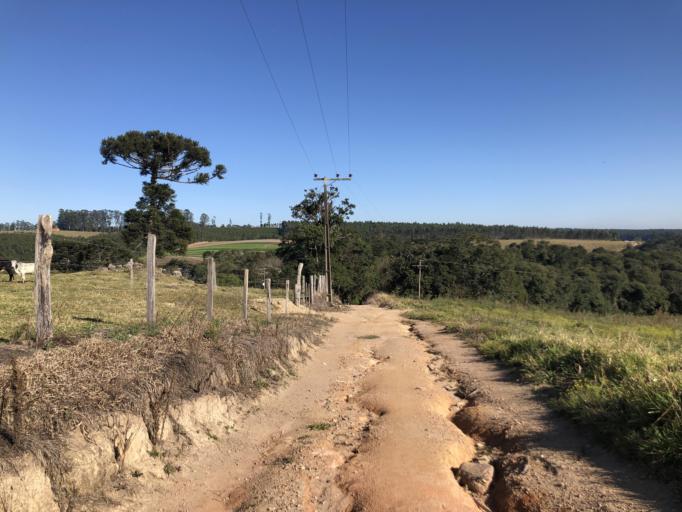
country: BR
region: Sao Paulo
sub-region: Pilar Do Sul
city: Pilar do Sul
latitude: -23.8295
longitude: -47.6247
